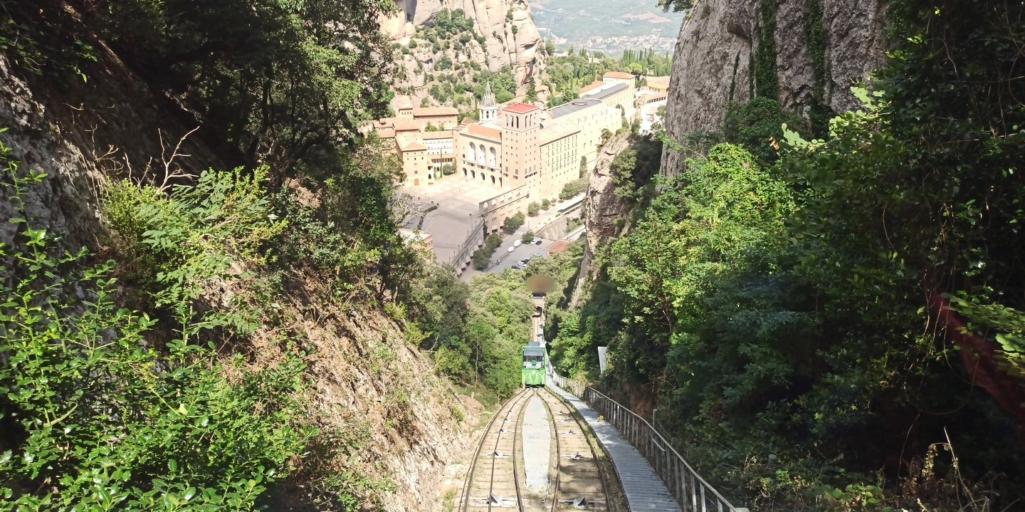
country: ES
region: Catalonia
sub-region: Provincia de Barcelona
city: Collbato
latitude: 41.5901
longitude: 1.8345
